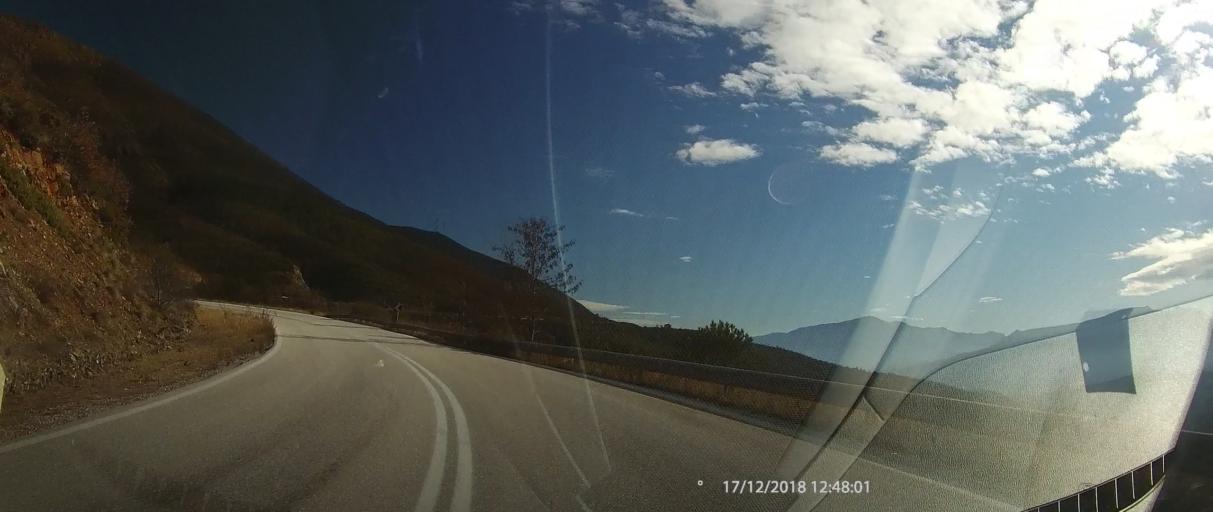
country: GR
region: Thessaly
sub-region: Trikala
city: Kastraki
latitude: 39.7856
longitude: 21.4323
